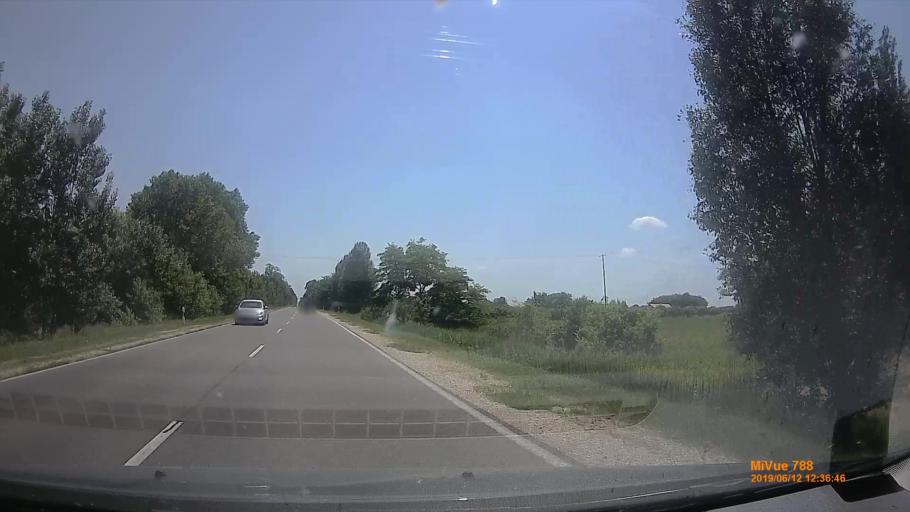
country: HU
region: Bacs-Kiskun
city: Varosfoeld
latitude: 46.7946
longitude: 19.7850
